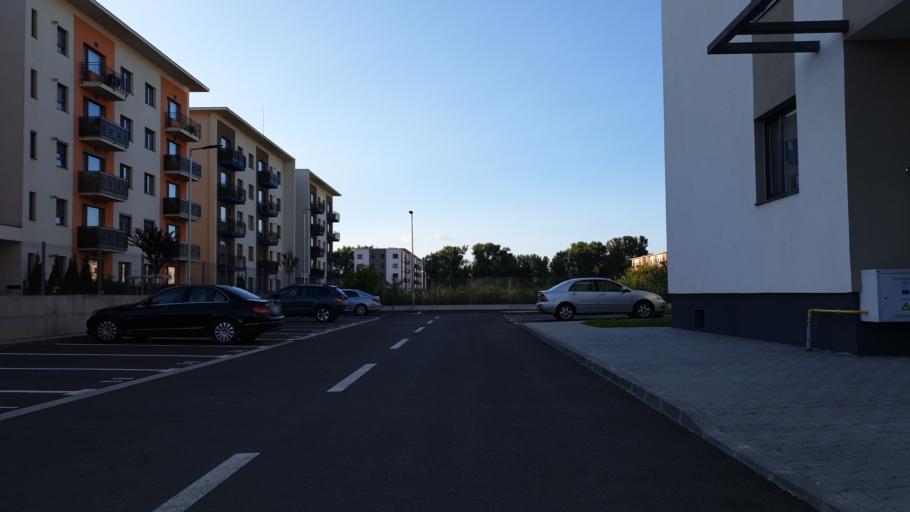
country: RO
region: Brasov
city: Brasov
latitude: 45.6798
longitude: 25.6072
